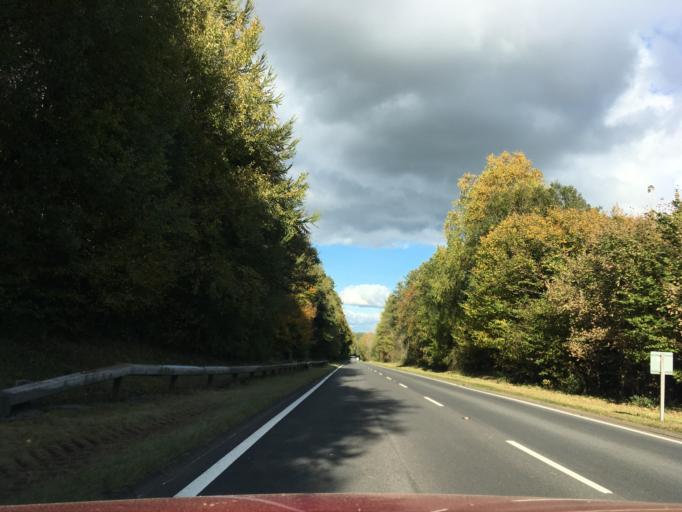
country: GB
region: Wales
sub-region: Sir Powys
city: Brecon
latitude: 51.8975
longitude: -3.4922
